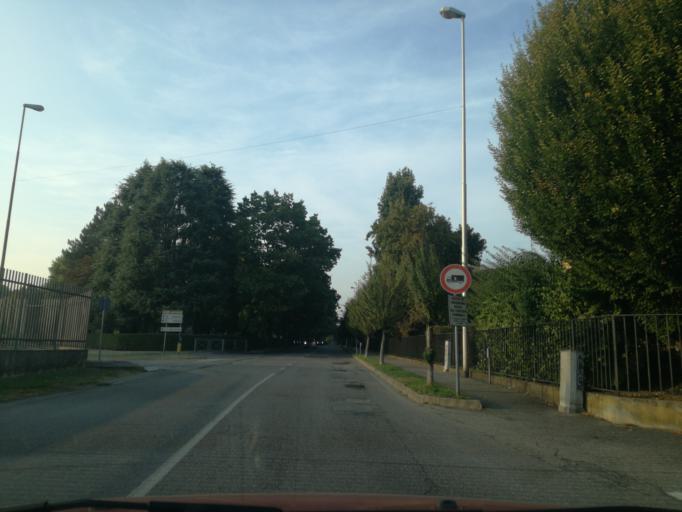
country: IT
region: Lombardy
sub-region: Provincia di Monza e Brianza
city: Carnate
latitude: 45.6480
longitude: 9.3861
